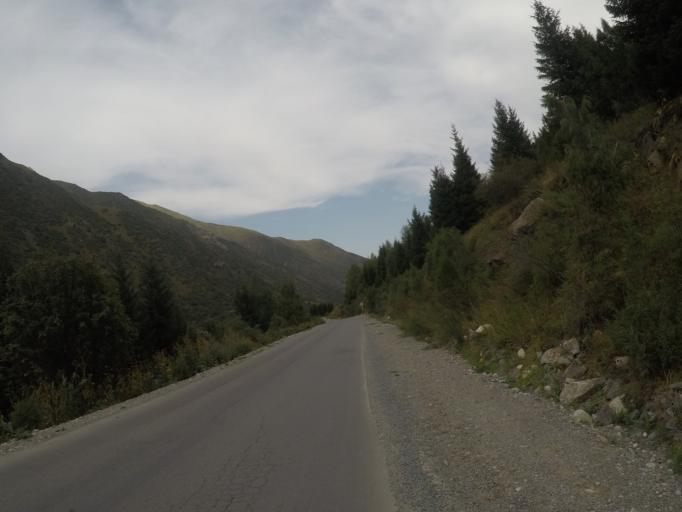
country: KG
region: Chuy
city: Bishkek
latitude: 42.5889
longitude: 74.4839
